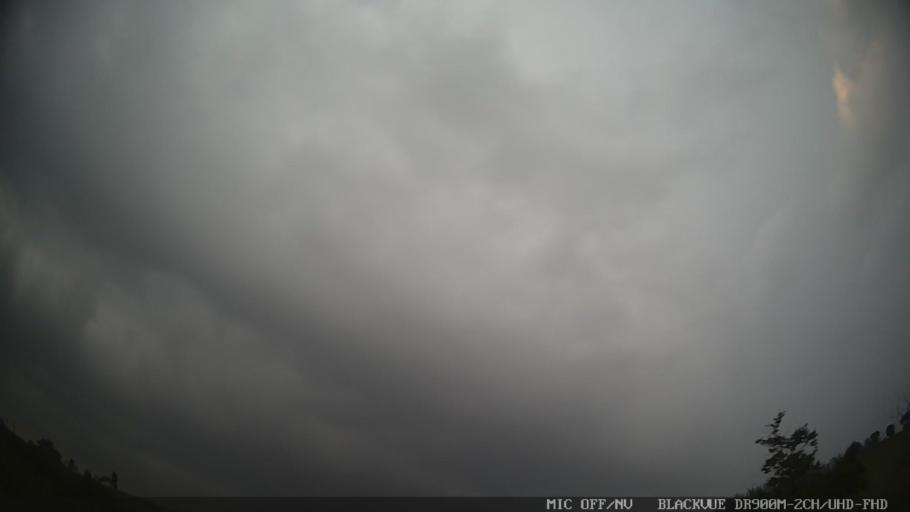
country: BR
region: Sao Paulo
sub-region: Braganca Paulista
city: Braganca Paulista
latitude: -22.9464
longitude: -46.6880
